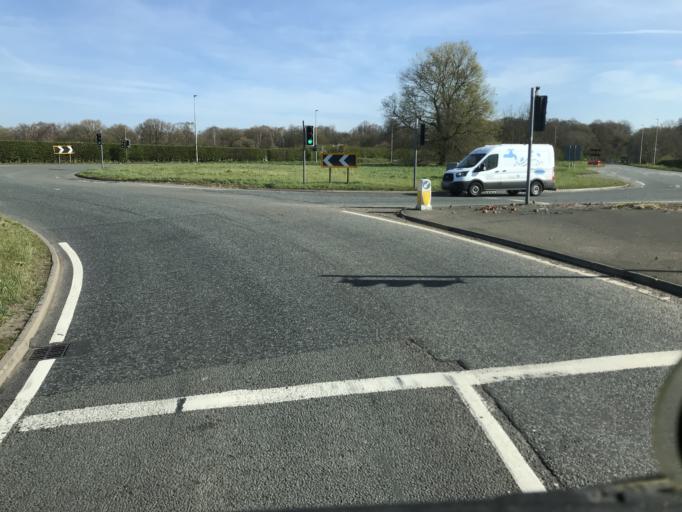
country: GB
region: England
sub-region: Cheshire West and Chester
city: Marston
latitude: 53.2739
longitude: -2.4516
